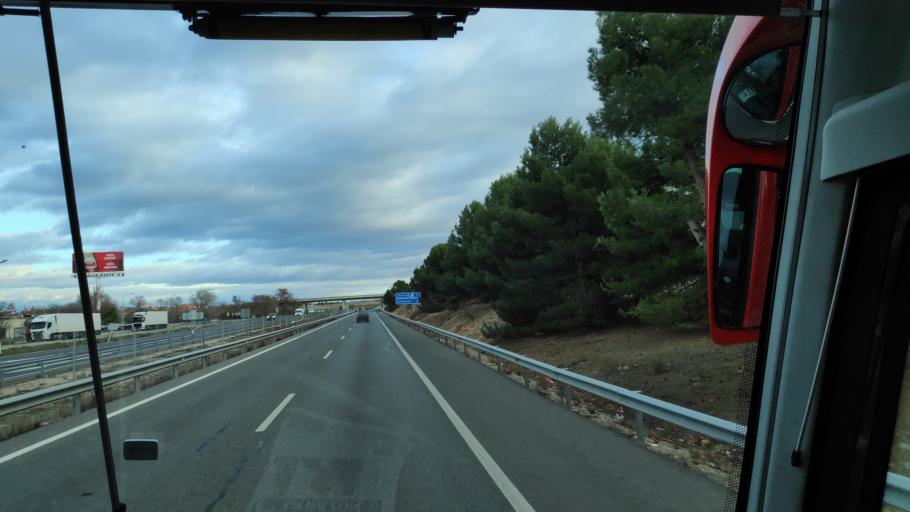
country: ES
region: Madrid
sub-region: Provincia de Madrid
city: Villarejo de Salvanes
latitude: 40.1674
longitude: -3.2857
